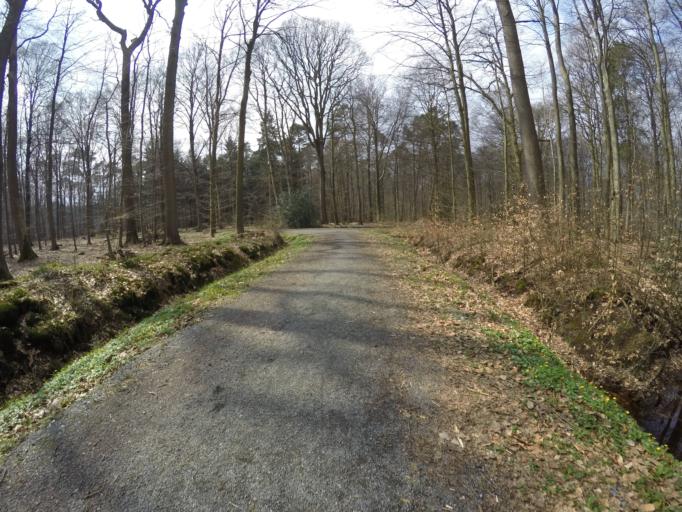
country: DE
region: Schleswig-Holstein
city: Ellerhoop
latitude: 53.7199
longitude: 9.7995
